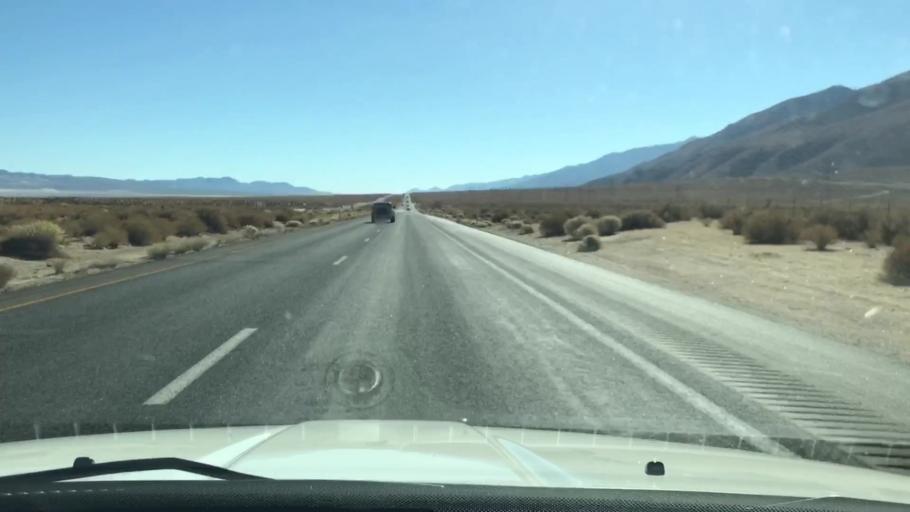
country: US
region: California
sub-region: Inyo County
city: Lone Pine
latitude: 36.4149
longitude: -118.0288
